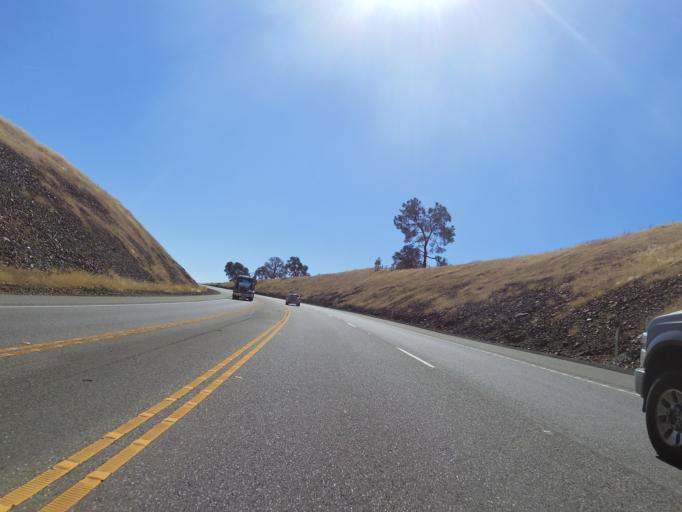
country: US
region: California
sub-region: Amador County
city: Sutter Creek
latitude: 38.4090
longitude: -120.8344
